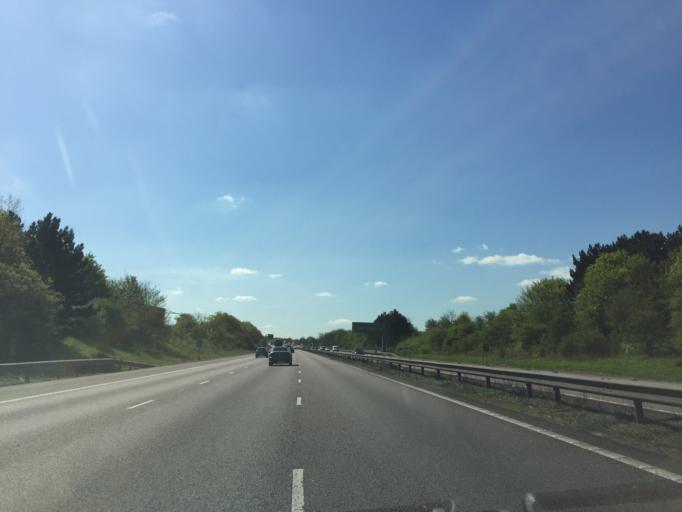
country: GB
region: England
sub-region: Essex
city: Epping
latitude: 51.7222
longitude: 0.1419
